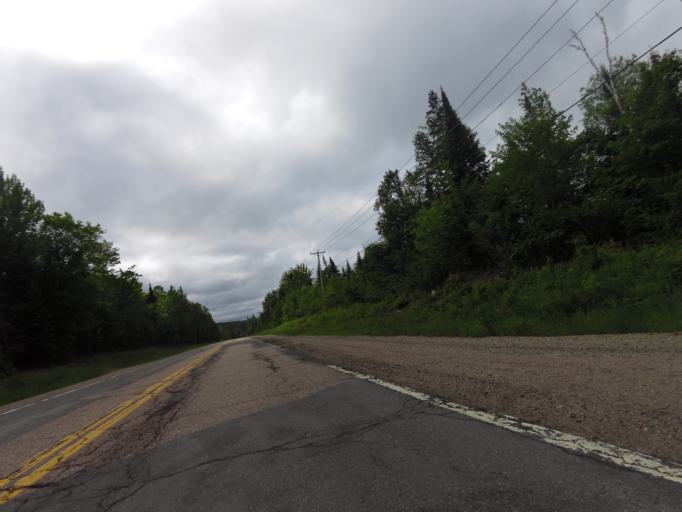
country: CA
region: Quebec
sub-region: Outaouais
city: Shawville
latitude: 45.8238
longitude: -76.4611
